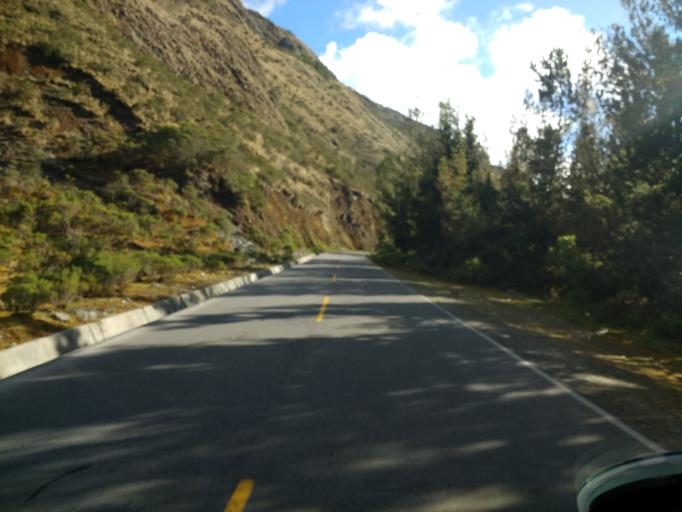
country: PE
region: Cusco
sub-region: Provincia de Urubamba
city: Ollantaytambo
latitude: -13.1218
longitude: -72.3299
